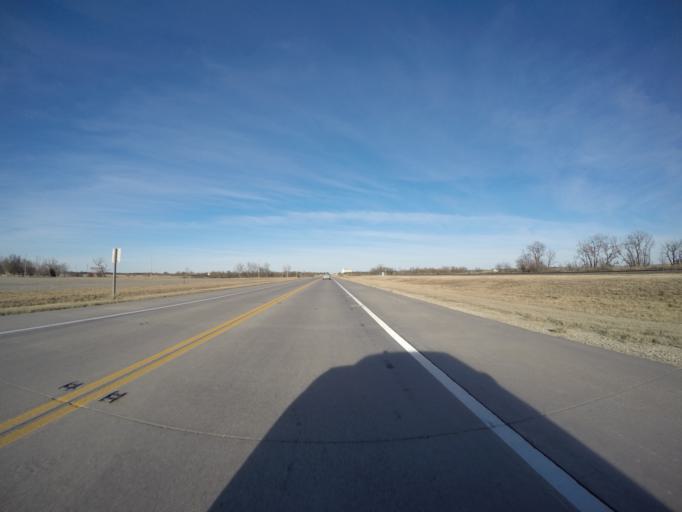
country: US
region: Kansas
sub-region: Harvey County
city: North Newton
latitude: 38.1010
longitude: -97.2755
